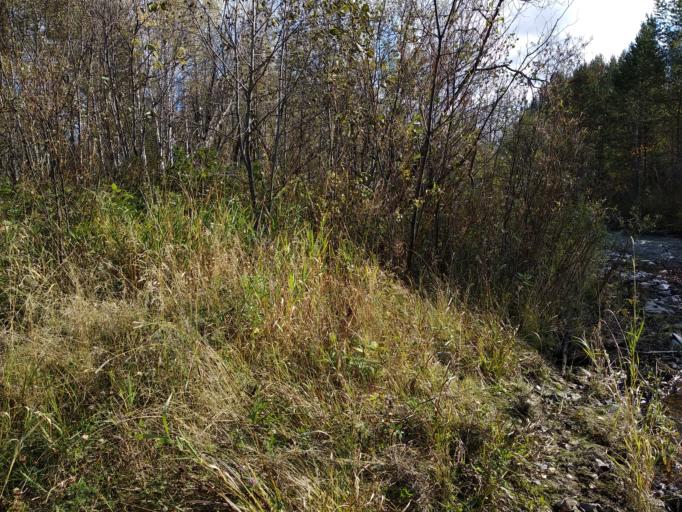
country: RU
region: Sverdlovsk
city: Krasnotur'insk
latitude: 59.9782
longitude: 60.4154
